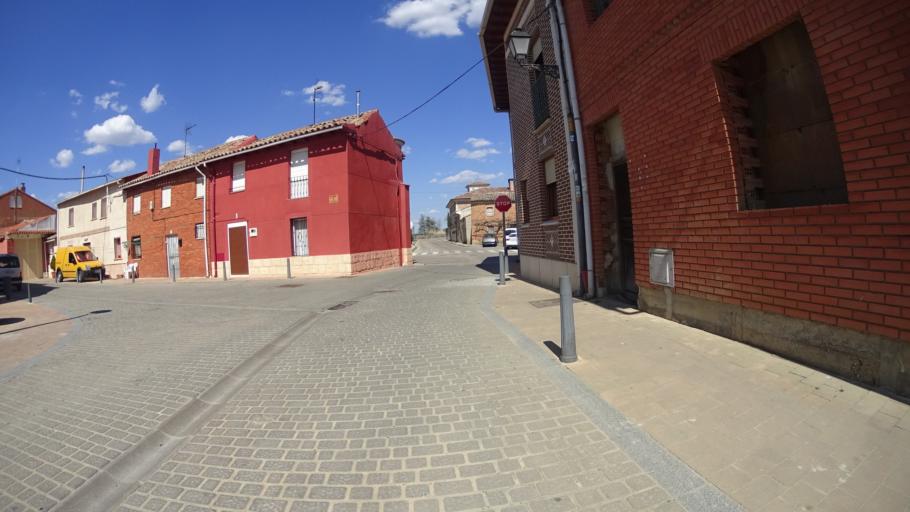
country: ES
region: Castille and Leon
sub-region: Provincia de Palencia
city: Grijota
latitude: 42.0539
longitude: -4.5810
